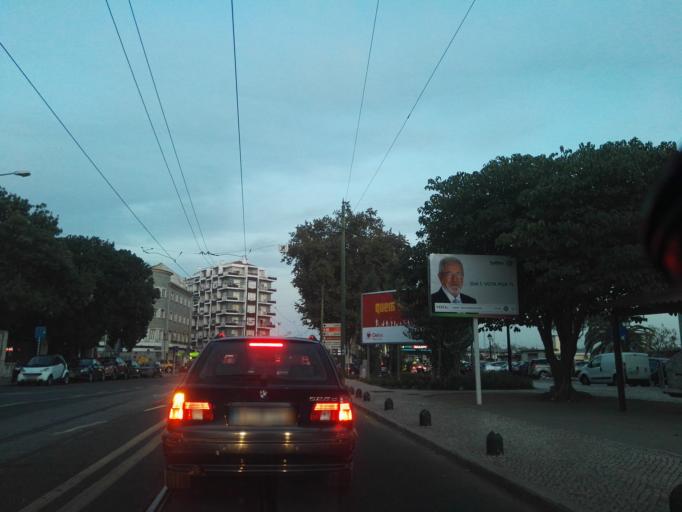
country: PT
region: Lisbon
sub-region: Oeiras
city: Alges
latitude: 38.6993
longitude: -9.2308
